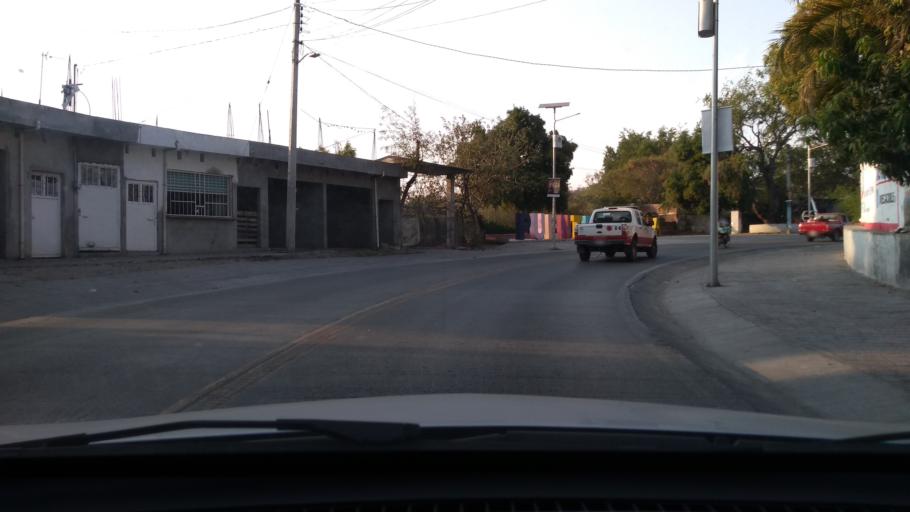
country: MX
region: Morelos
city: Puente de Ixtla
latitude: 18.6323
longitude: -99.3241
